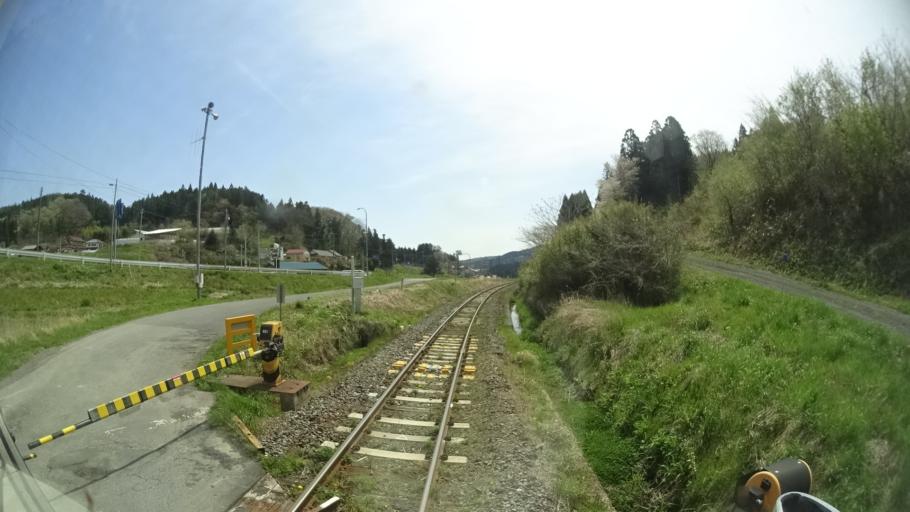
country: JP
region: Iwate
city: Ichinoseki
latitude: 38.9373
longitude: 141.4135
